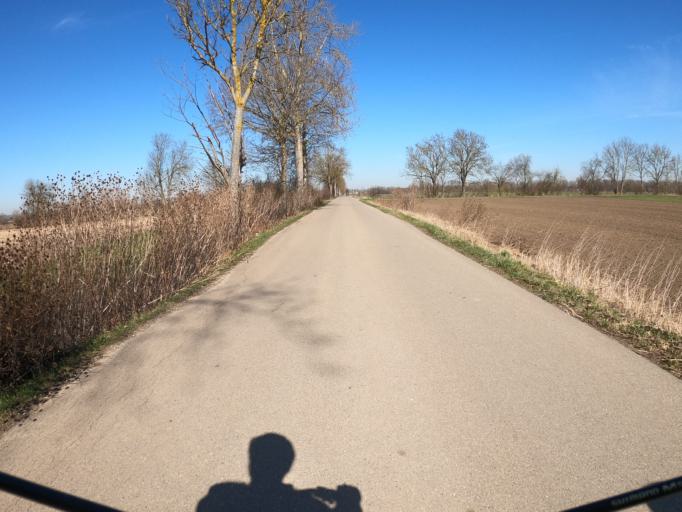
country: DE
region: Baden-Wuerttemberg
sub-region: Tuebingen Region
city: Langenau
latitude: 48.4662
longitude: 10.1422
